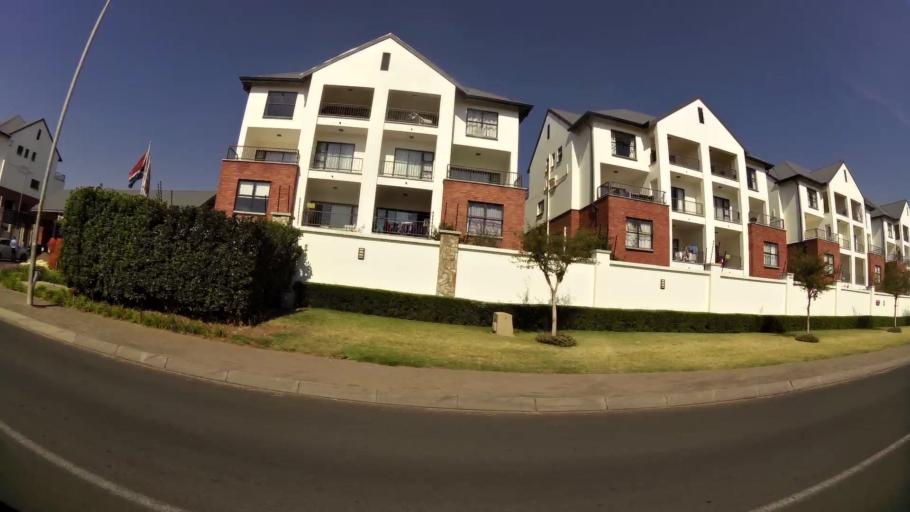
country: ZA
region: Gauteng
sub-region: City of Johannesburg Metropolitan Municipality
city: Modderfontein
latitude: -26.1178
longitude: 28.1592
